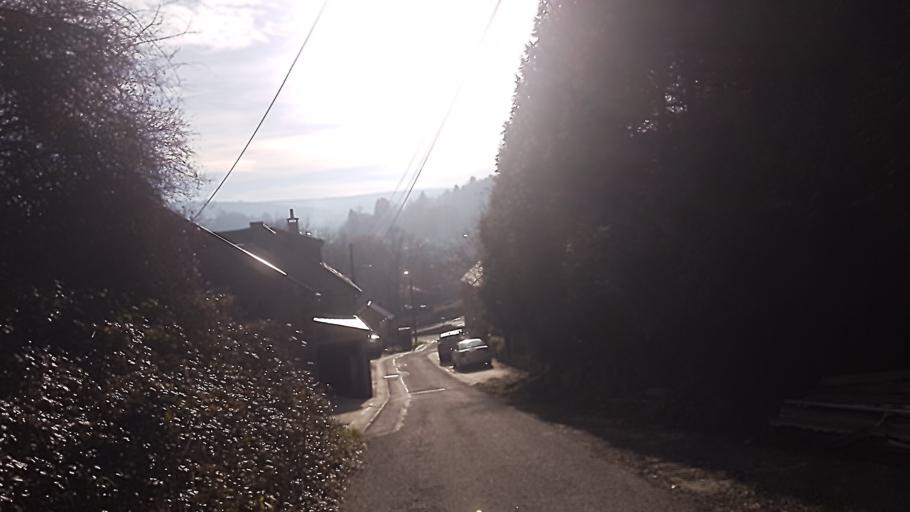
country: BE
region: Wallonia
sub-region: Province de Namur
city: Couvin
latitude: 50.0768
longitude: 4.6068
